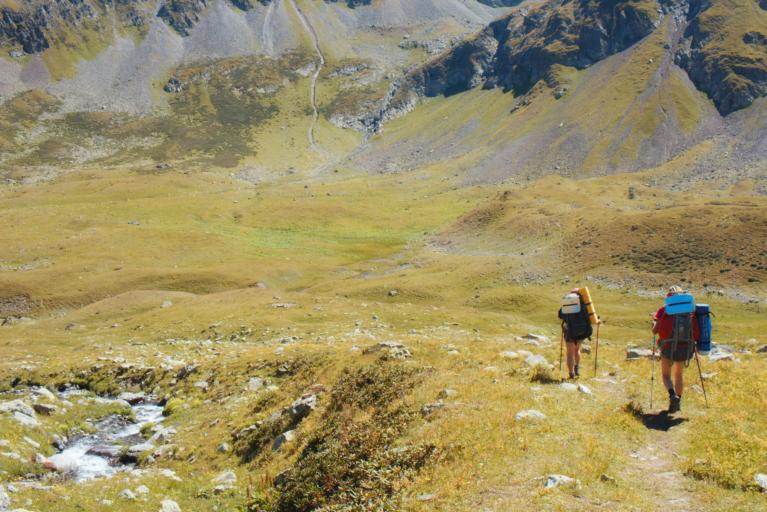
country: RU
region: Karachayevo-Cherkesiya
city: Mednogorskiy
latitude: 43.6231
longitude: 41.1158
